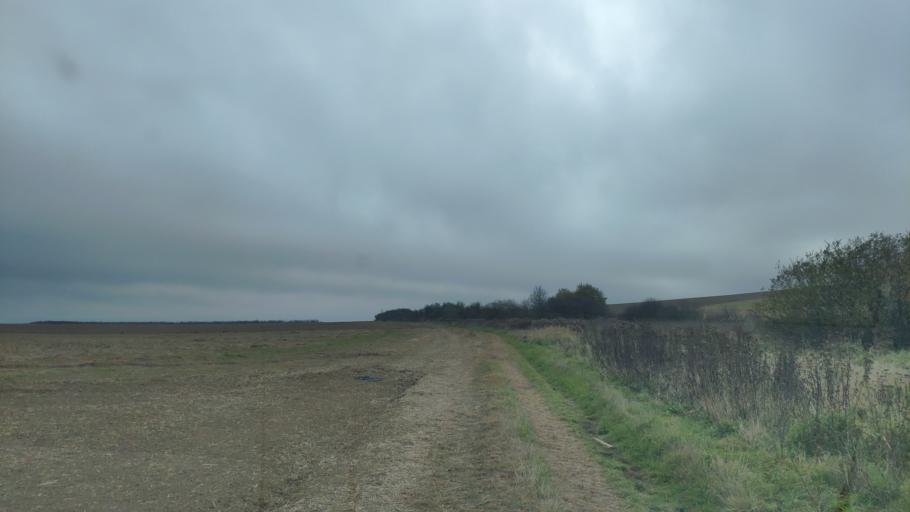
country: SK
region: Presovsky
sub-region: Okres Presov
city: Presov
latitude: 49.0161
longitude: 21.2062
